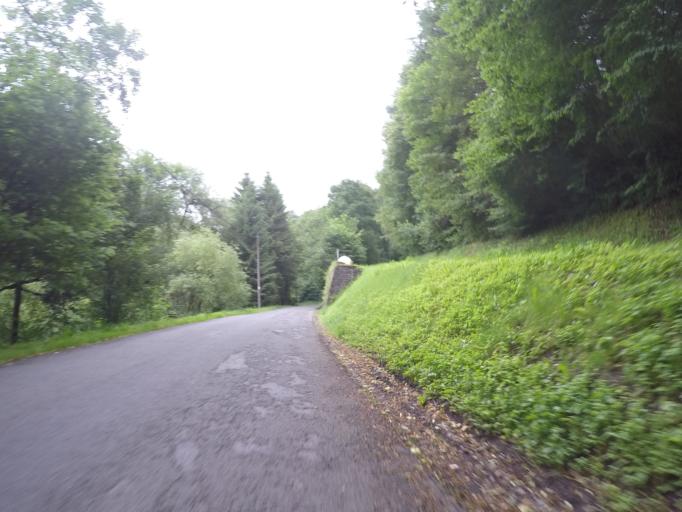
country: BE
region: Wallonia
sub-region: Province de Namur
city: Yvoir
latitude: 50.3463
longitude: 4.9479
